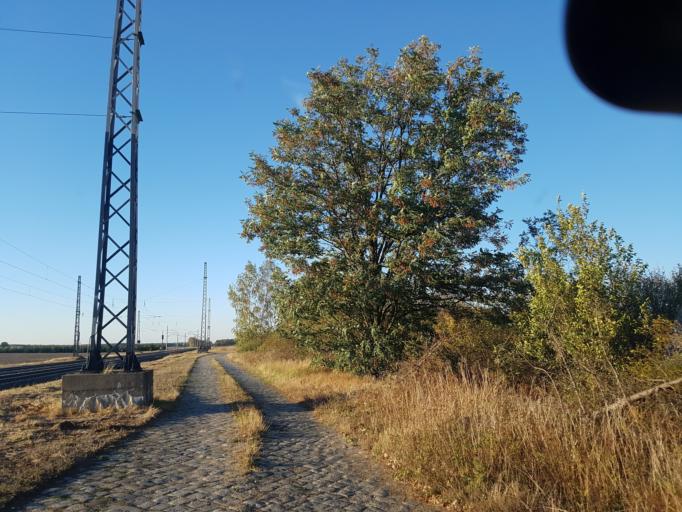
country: DE
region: Brandenburg
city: Muhlberg
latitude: 51.5023
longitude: 13.2803
